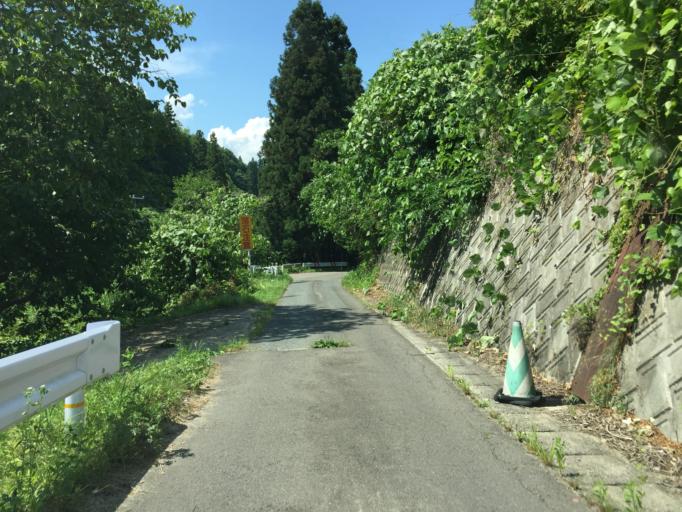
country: JP
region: Fukushima
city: Yanagawamachi-saiwaicho
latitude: 37.7819
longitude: 140.6539
